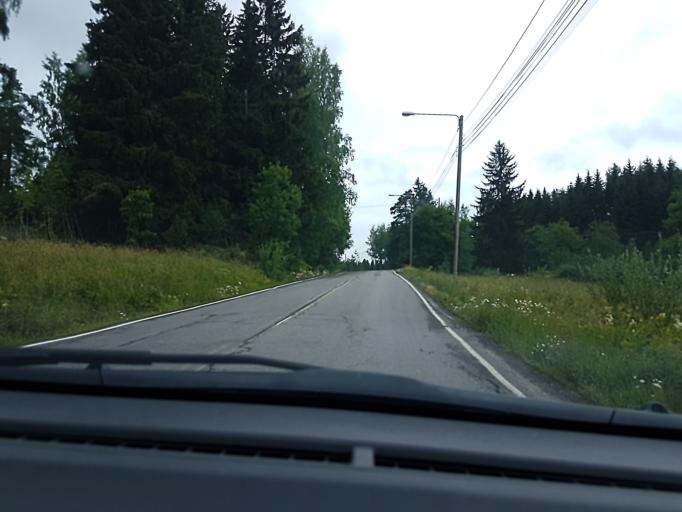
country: FI
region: Uusimaa
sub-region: Helsinki
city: Pornainen
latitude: 60.4353
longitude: 25.3853
